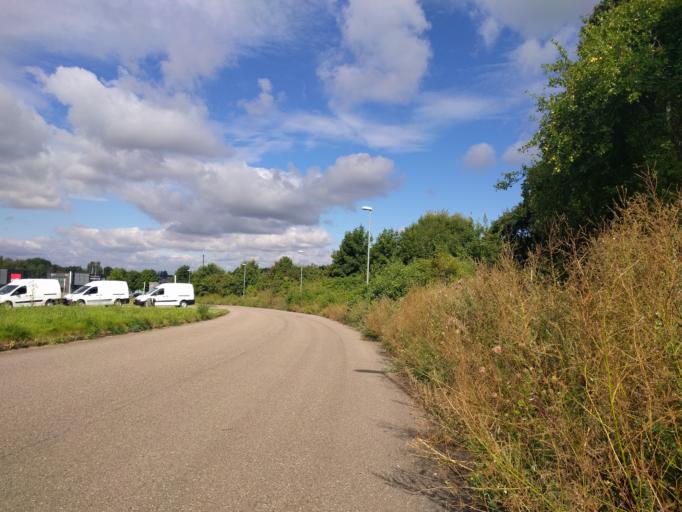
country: DK
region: South Denmark
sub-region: Fredericia Kommune
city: Snoghoj
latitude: 55.5319
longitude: 9.7219
